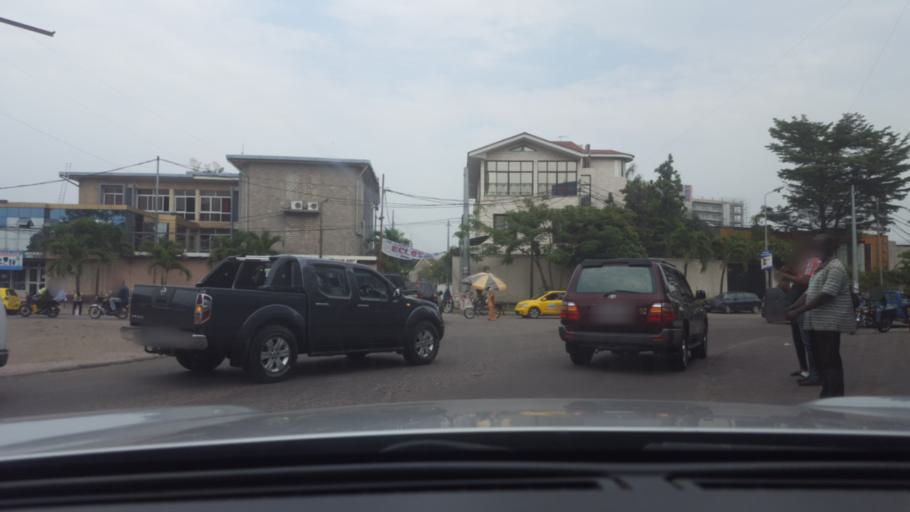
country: CD
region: Kinshasa
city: Kinshasa
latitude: -4.3231
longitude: 15.2780
